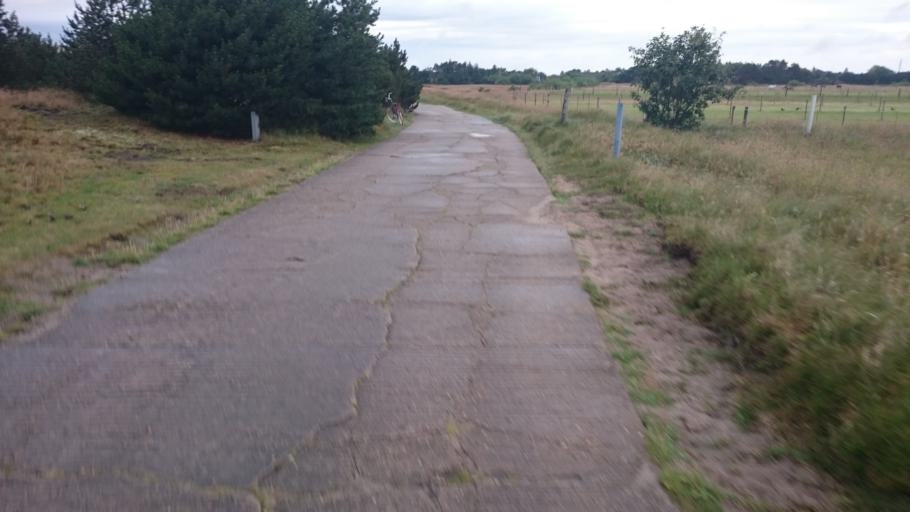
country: DK
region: South Denmark
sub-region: Fano Kommune
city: Nordby
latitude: 55.4335
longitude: 8.3875
